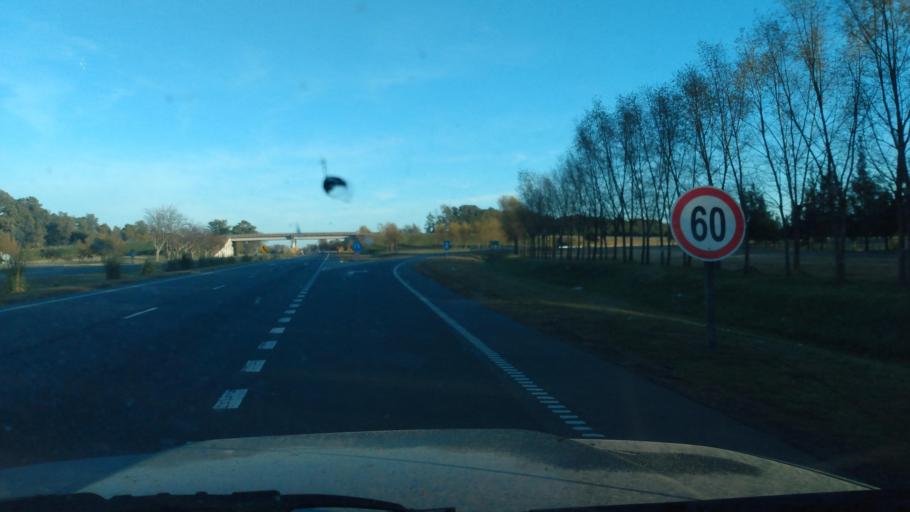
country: AR
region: Buenos Aires
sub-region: Partido de Lujan
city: Lujan
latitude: -34.5389
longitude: -59.2537
